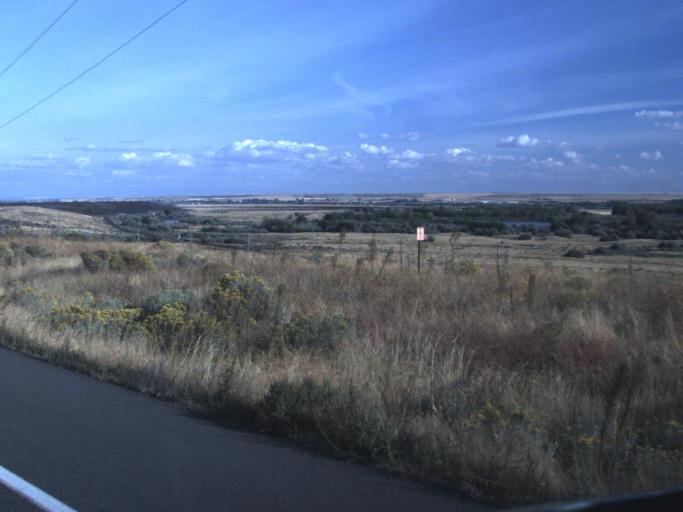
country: US
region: Oregon
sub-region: Morrow County
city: Irrigon
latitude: 45.9419
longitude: -119.5536
